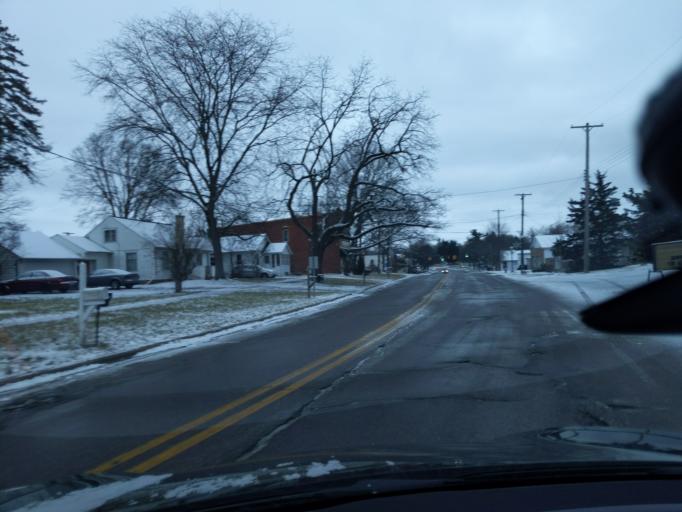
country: US
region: Michigan
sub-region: Ingham County
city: Okemos
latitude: 42.7176
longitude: -84.4313
